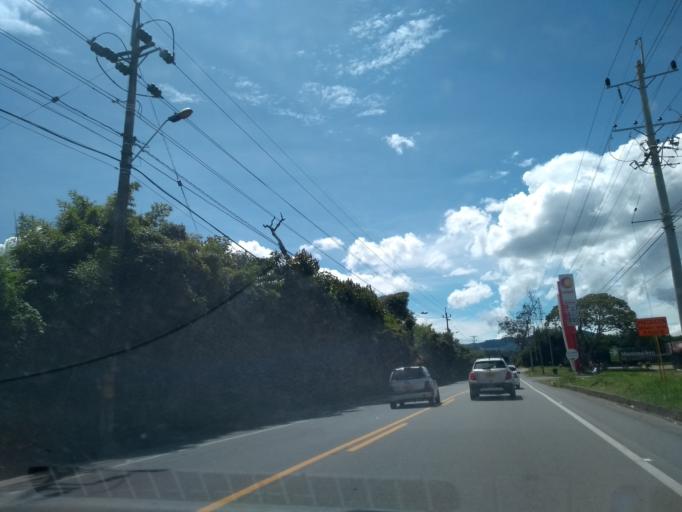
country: CO
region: Antioquia
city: La Ceja
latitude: 6.0467
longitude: -75.3966
